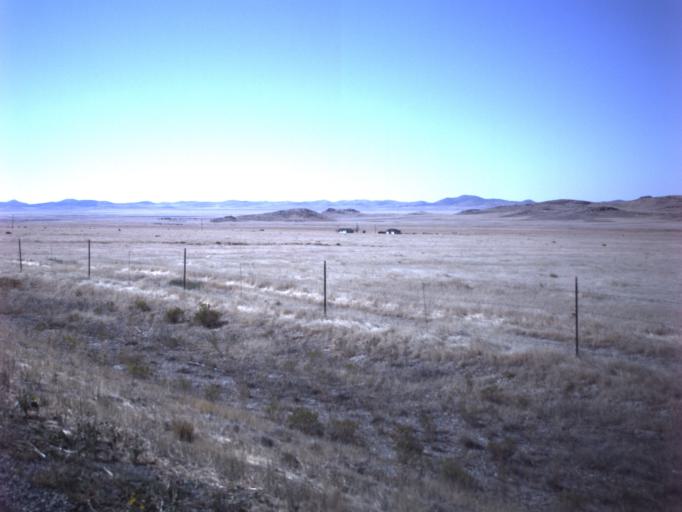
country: US
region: Utah
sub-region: Tooele County
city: Grantsville
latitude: 40.4029
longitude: -112.7481
